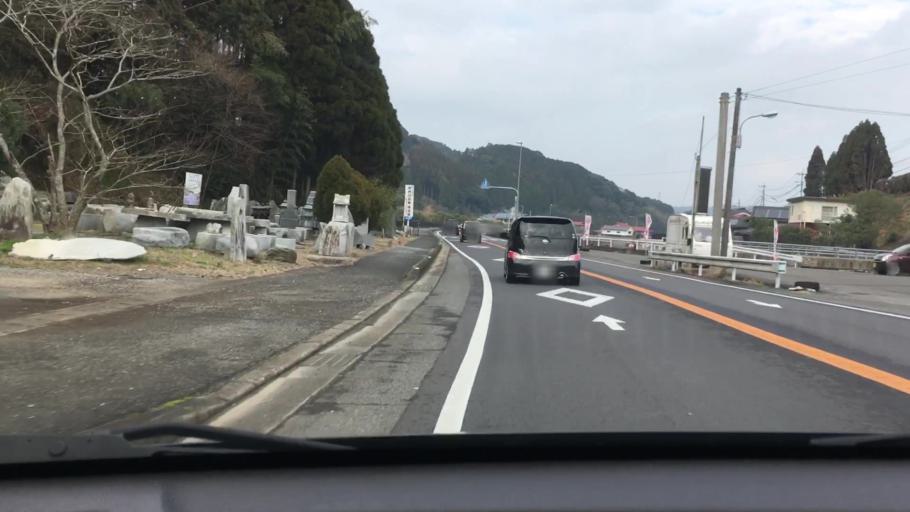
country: JP
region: Saga Prefecture
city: Imaricho-ko
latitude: 33.3222
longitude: 129.9292
